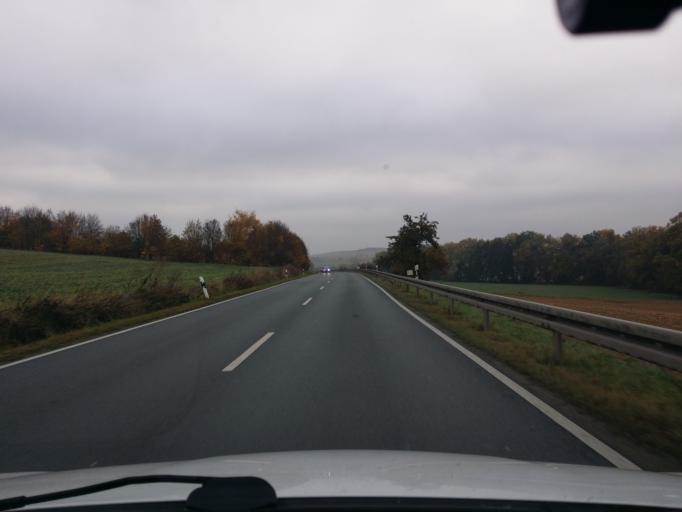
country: DE
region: Hesse
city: Bad Camberg
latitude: 50.2783
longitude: 8.2811
